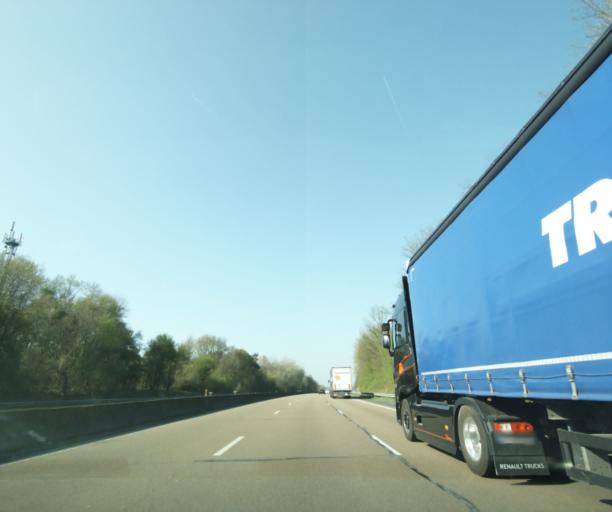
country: FR
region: Ile-de-France
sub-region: Departement de Seine-et-Marne
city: Cely
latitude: 48.4641
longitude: 2.5165
